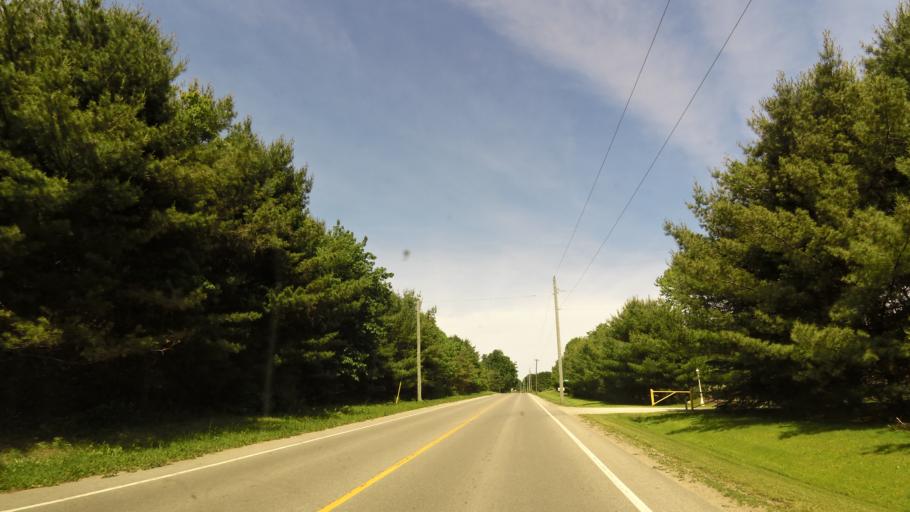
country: CA
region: Ontario
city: Norfolk County
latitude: 42.6746
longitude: -80.3837
